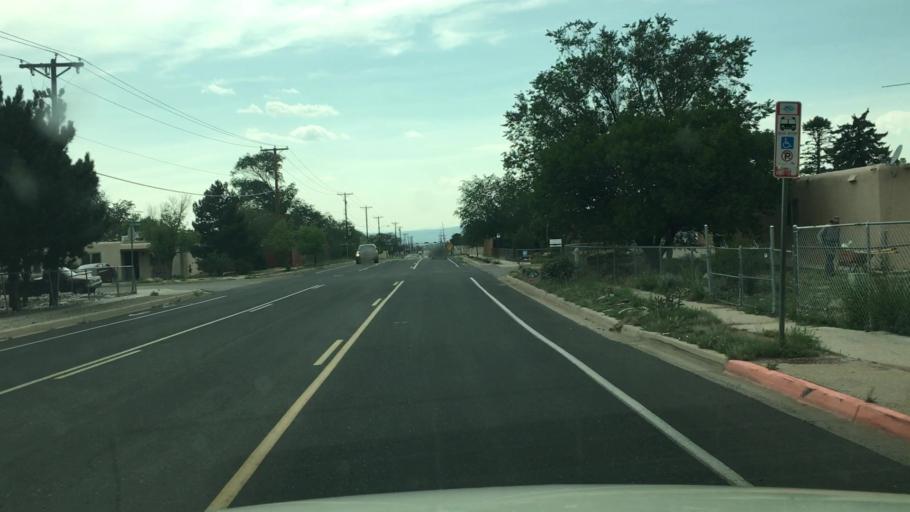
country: US
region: New Mexico
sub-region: Santa Fe County
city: Santa Fe
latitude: 35.6521
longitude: -105.9617
